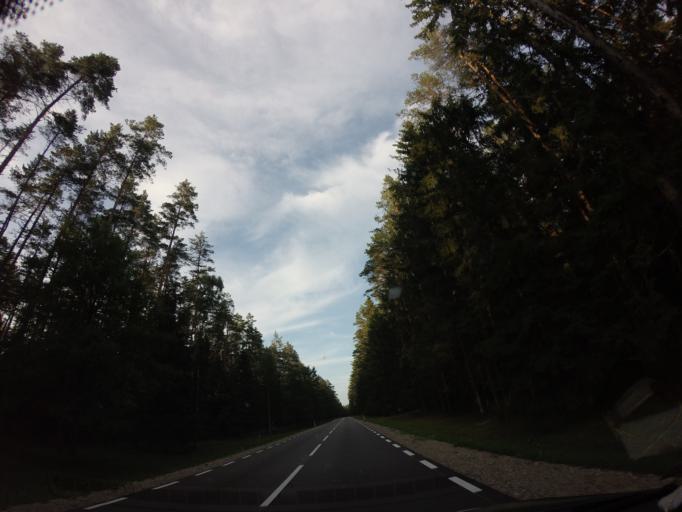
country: PL
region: Podlasie
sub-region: Powiat sejnenski
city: Krasnopol
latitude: 53.9712
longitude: 23.2554
